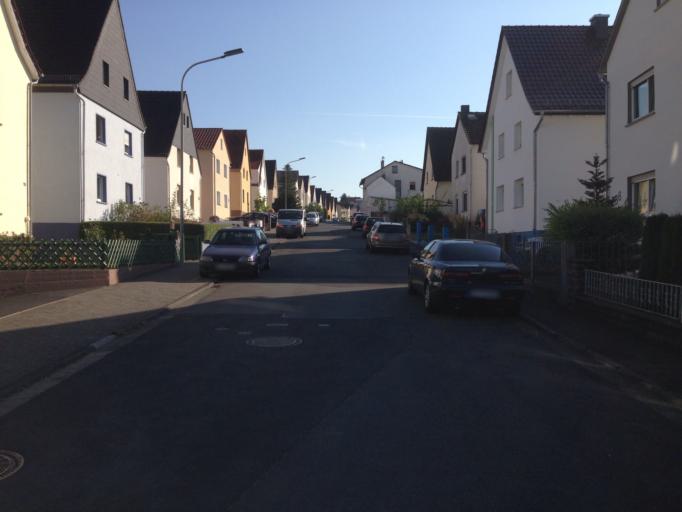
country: DE
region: Hesse
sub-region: Regierungsbezirk Giessen
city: Giessen
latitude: 50.5420
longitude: 8.7215
